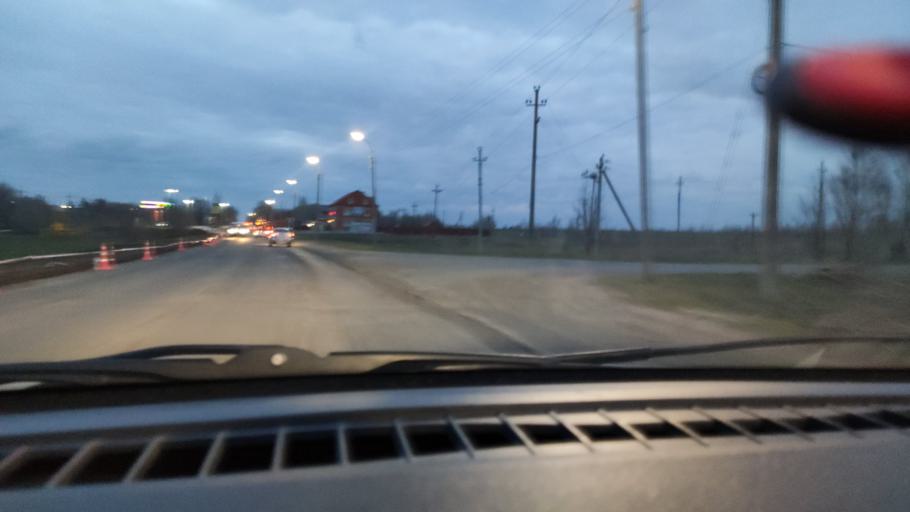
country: RU
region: Orenburg
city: Tatarskaya Kargala
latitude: 51.8688
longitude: 55.1430
